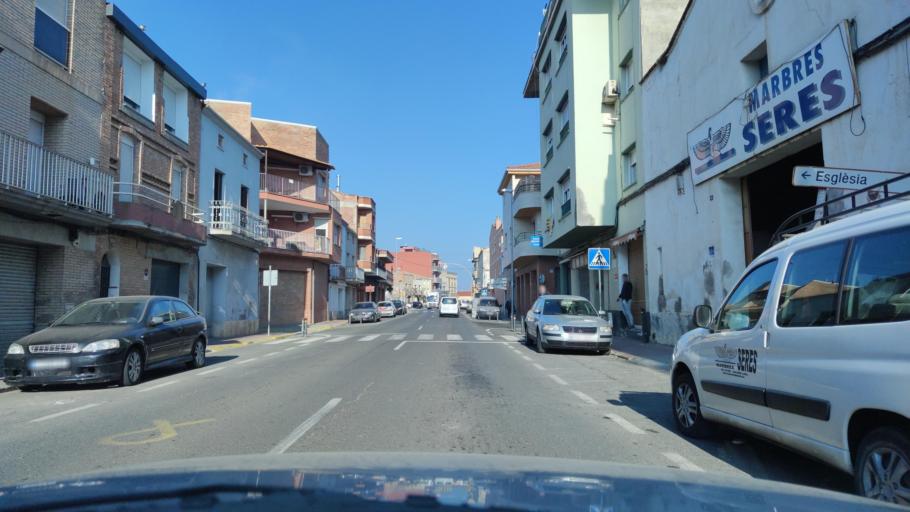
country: ES
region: Catalonia
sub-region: Provincia de Lleida
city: Lleida
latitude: 41.5723
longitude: 0.6052
